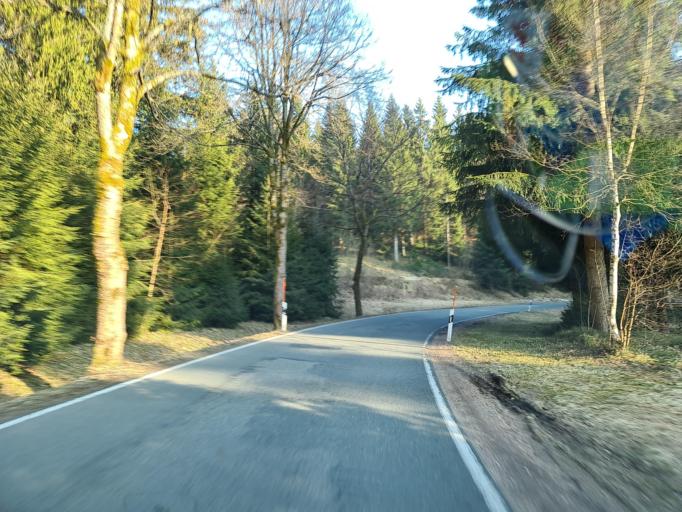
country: DE
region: Saxony
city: Schoenheide
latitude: 50.4726
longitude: 12.5227
